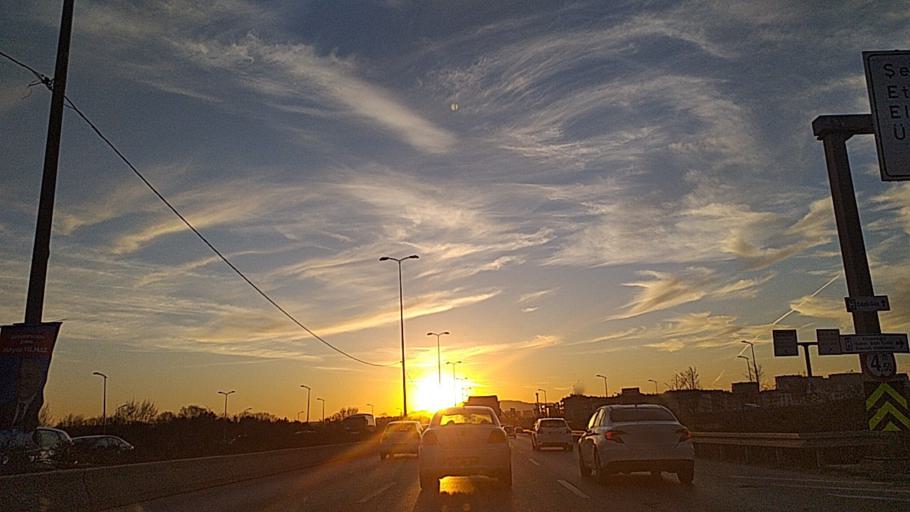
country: TR
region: Ankara
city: Etimesgut
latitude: 39.9631
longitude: 32.6696
